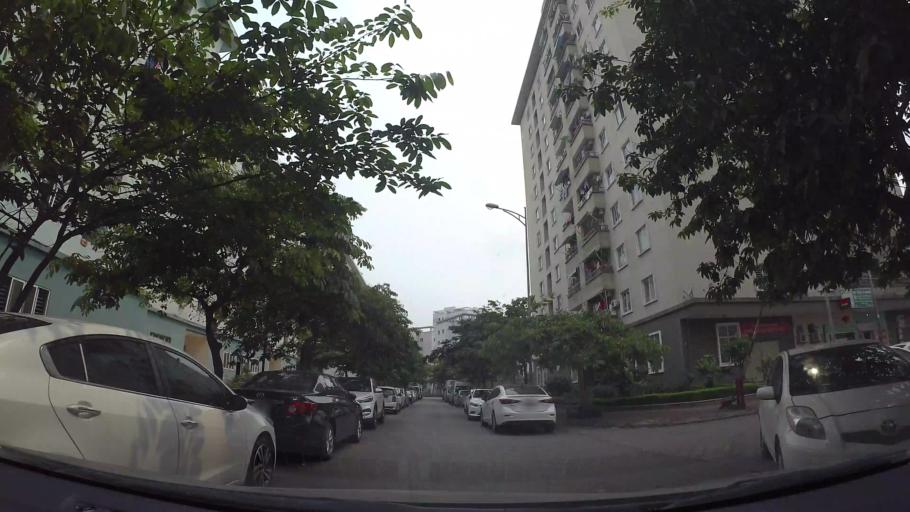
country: VN
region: Ha Noi
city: Trau Quy
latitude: 21.0577
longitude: 105.9125
